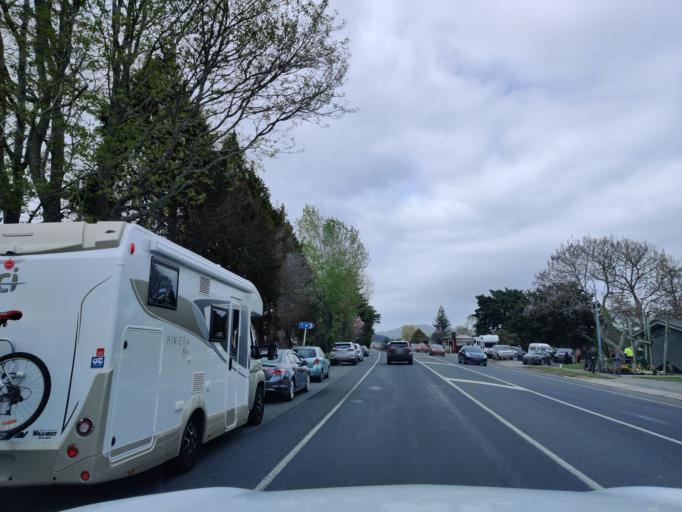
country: NZ
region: Waikato
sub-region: Waikato District
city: Ngaruawahia
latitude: -37.5488
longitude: 175.1585
